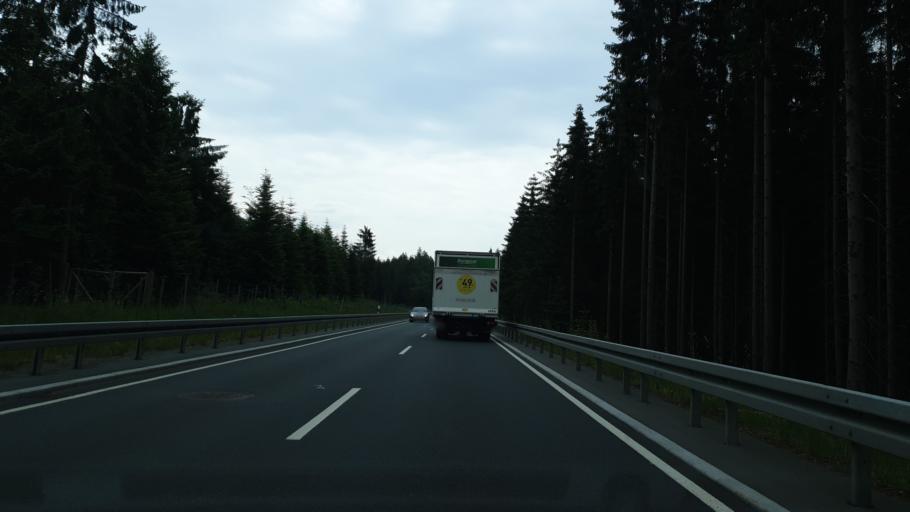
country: DE
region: Saxony
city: Tannenbergsthal
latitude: 50.4669
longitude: 12.4358
